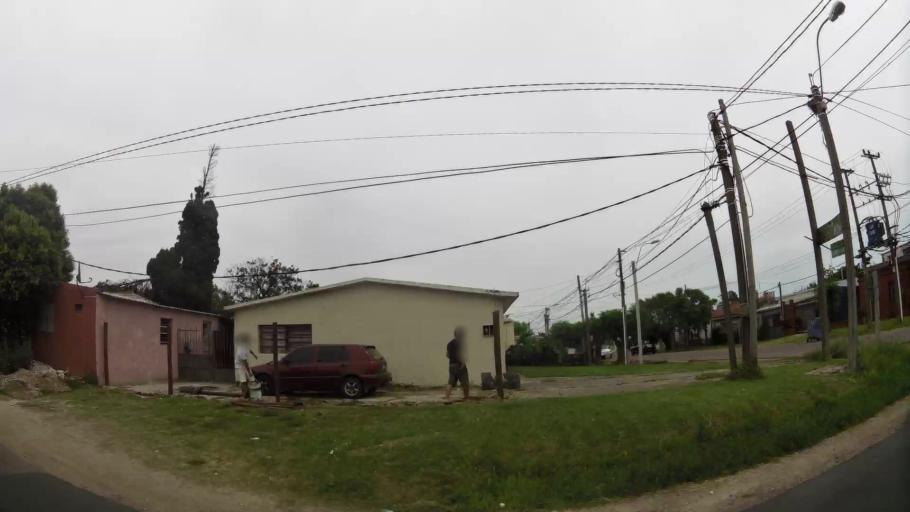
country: UY
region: Canelones
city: Las Piedras
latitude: -34.7343
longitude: -56.2276
